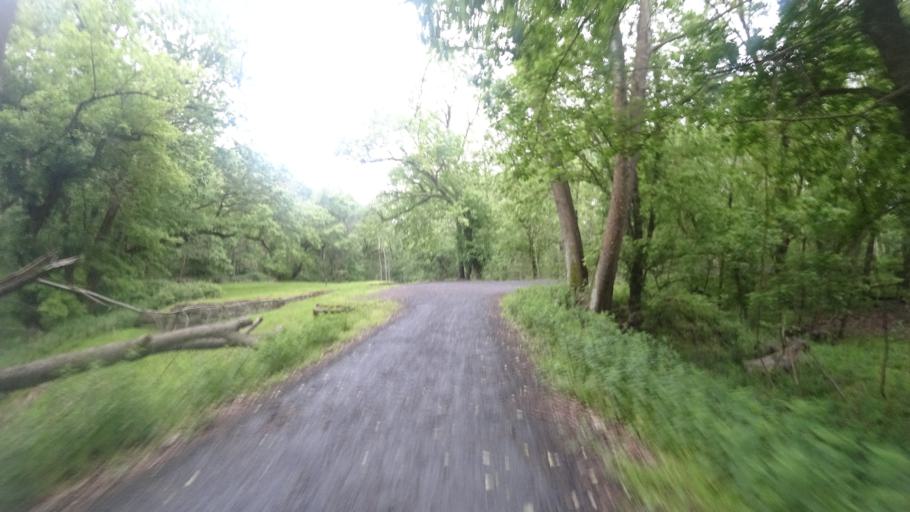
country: US
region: West Virginia
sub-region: Jefferson County
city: Bolivar
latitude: 39.3370
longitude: -77.7535
